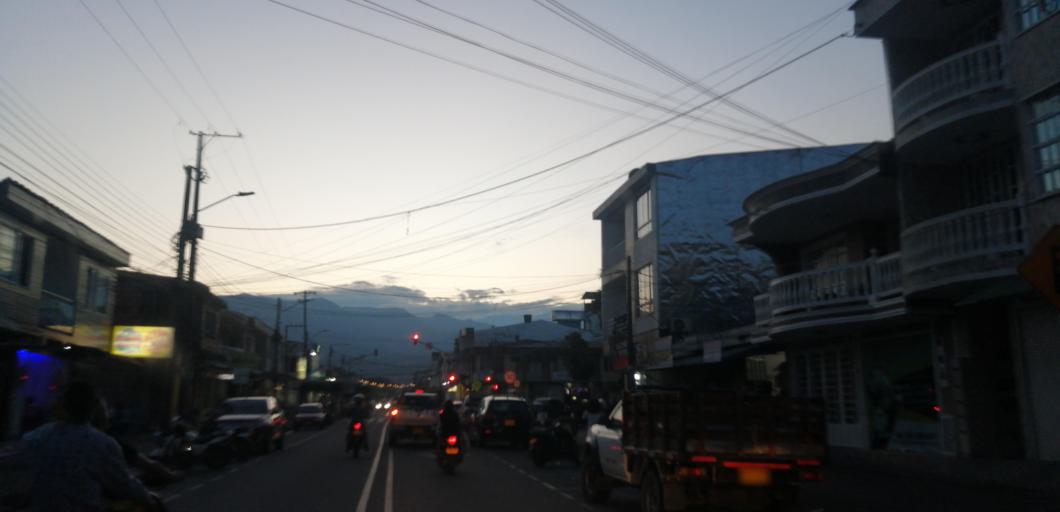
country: CO
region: Meta
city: Acacias
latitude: 3.9880
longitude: -73.7726
